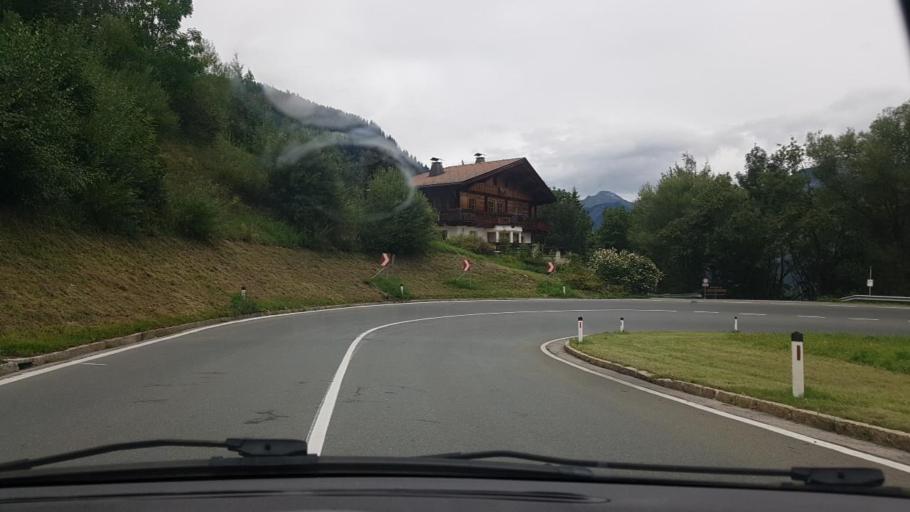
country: AT
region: Carinthia
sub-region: Politischer Bezirk Spittal an der Drau
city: Winklern
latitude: 46.8682
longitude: 12.8697
